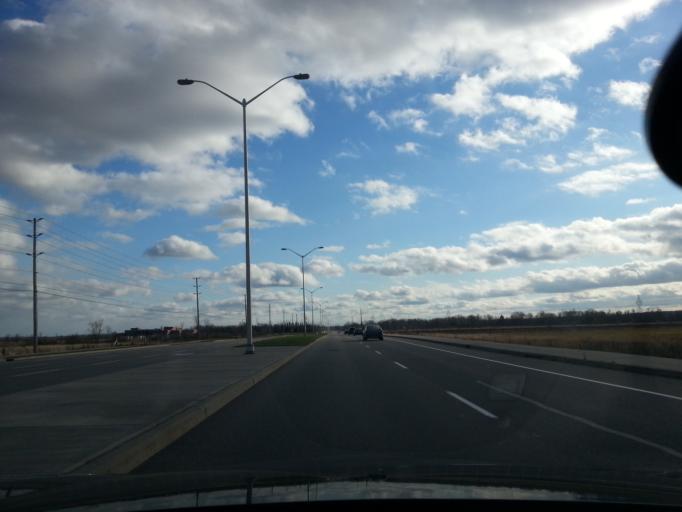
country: CA
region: Ontario
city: Ottawa
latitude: 45.2966
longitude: -75.6764
